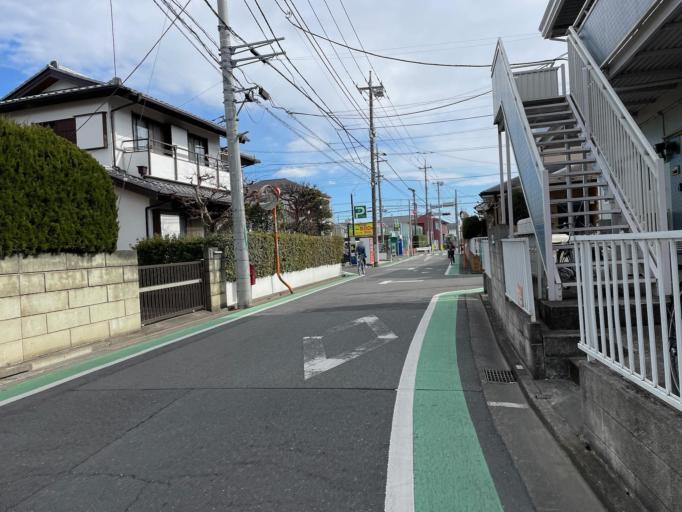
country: JP
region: Tokyo
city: Chofugaoka
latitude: 35.6384
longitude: 139.5678
